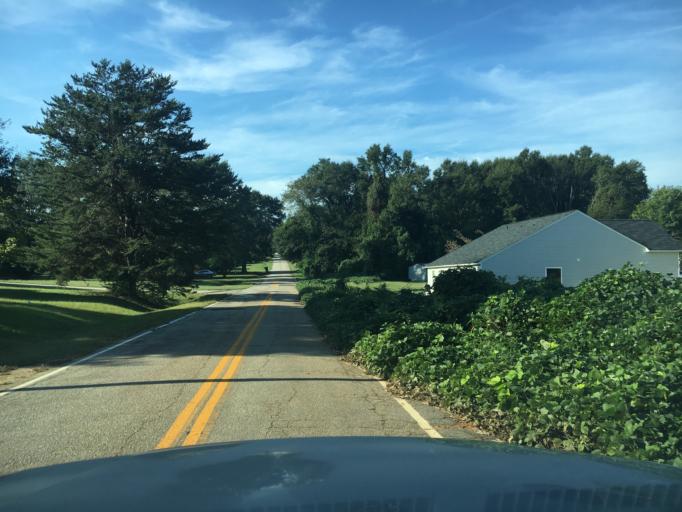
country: US
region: South Carolina
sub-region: Spartanburg County
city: Lyman
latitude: 34.9378
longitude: -82.1315
